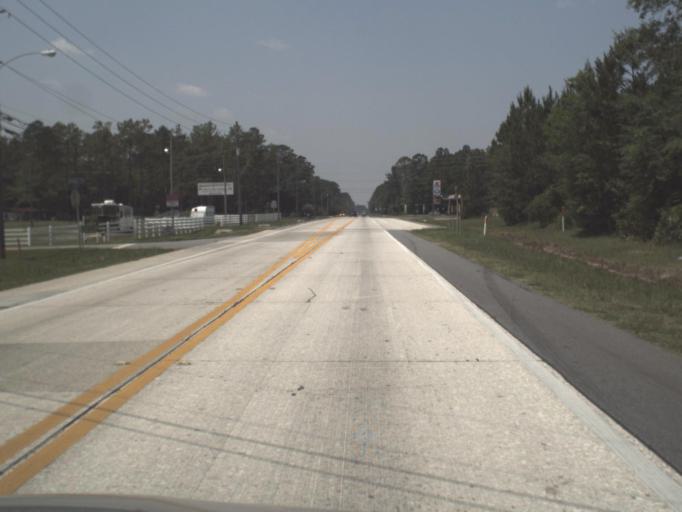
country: US
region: Florida
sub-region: Duval County
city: Baldwin
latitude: 30.2195
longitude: -81.9386
